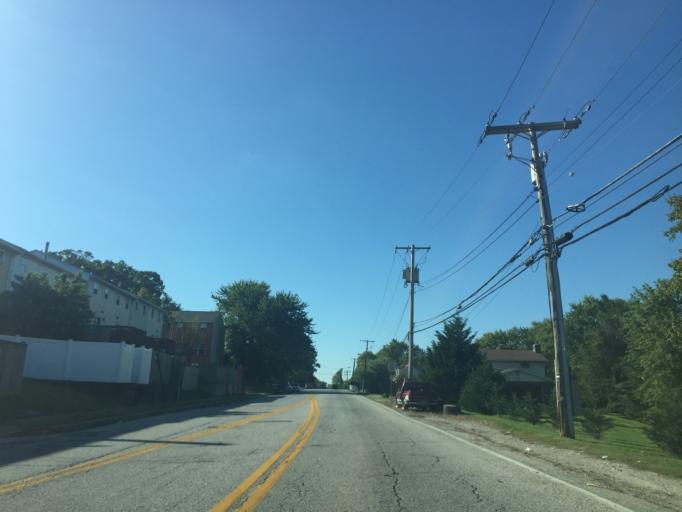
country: US
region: Maryland
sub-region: Baltimore County
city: Rossville
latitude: 39.3548
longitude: -76.4632
